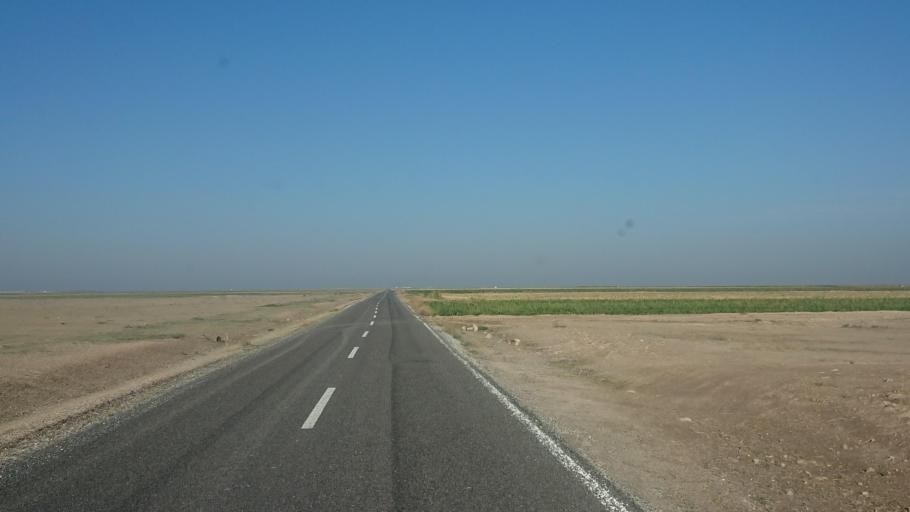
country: TR
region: Aksaray
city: Yesilova
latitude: 38.3876
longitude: 33.7932
